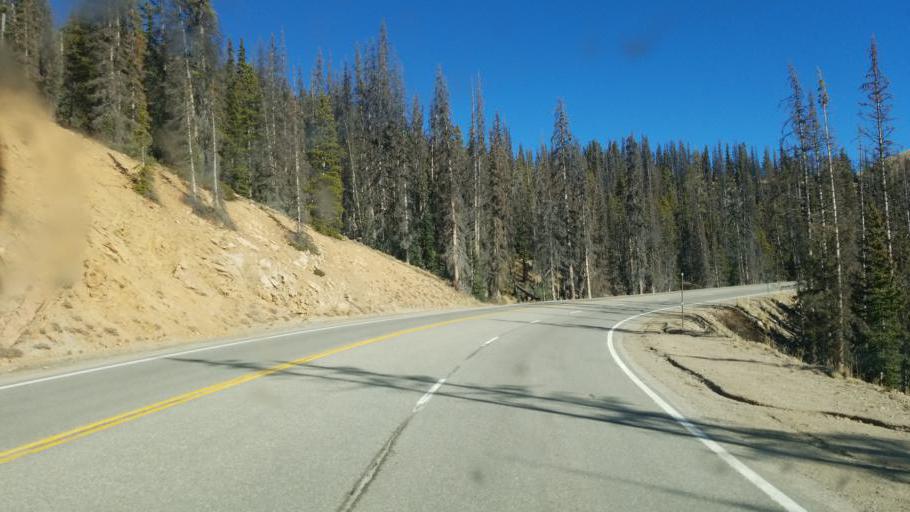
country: US
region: Colorado
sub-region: Chaffee County
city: Salida
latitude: 38.4895
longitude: -106.3284
